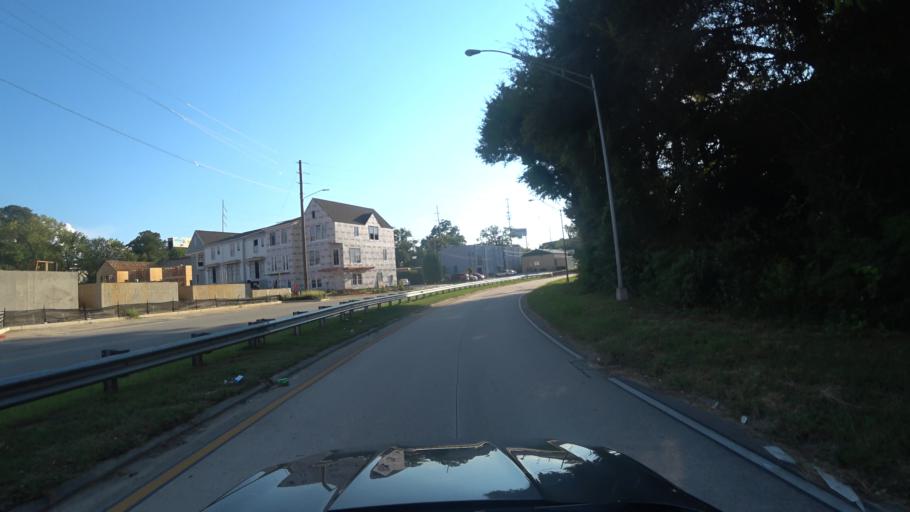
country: US
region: Georgia
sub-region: DeKalb County
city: Druid Hills
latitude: 33.8118
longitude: -84.3651
